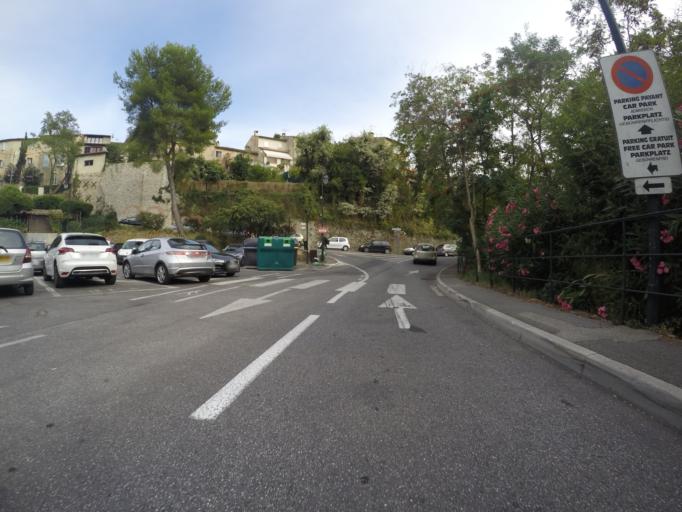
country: FR
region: Provence-Alpes-Cote d'Azur
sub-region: Departement des Alpes-Maritimes
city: Cagnes-sur-Mer
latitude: 43.6698
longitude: 7.1452
